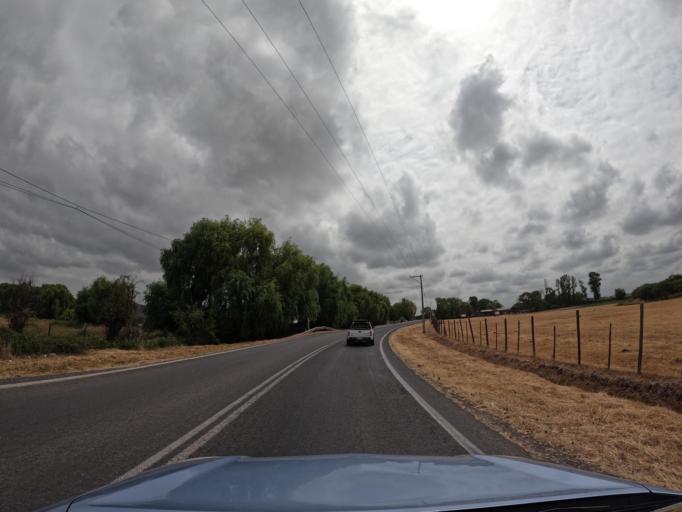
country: CL
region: Maule
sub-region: Provincia de Curico
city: Teno
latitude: -34.8496
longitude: -71.1924
